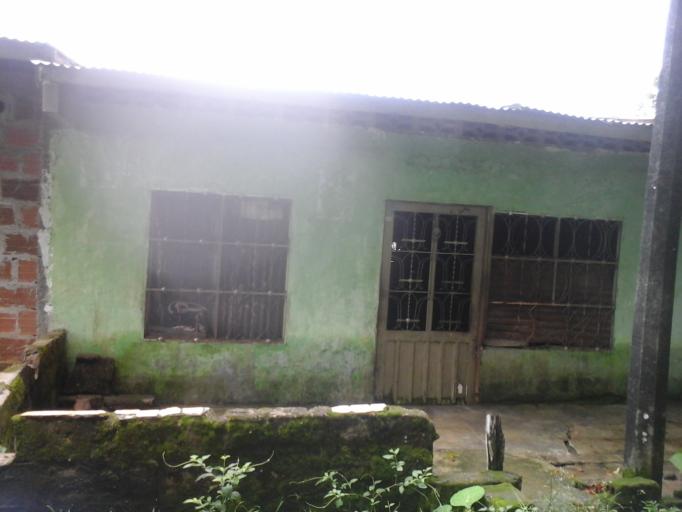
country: CO
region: Caqueta
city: El Doncello
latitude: 1.6104
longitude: -74.9987
